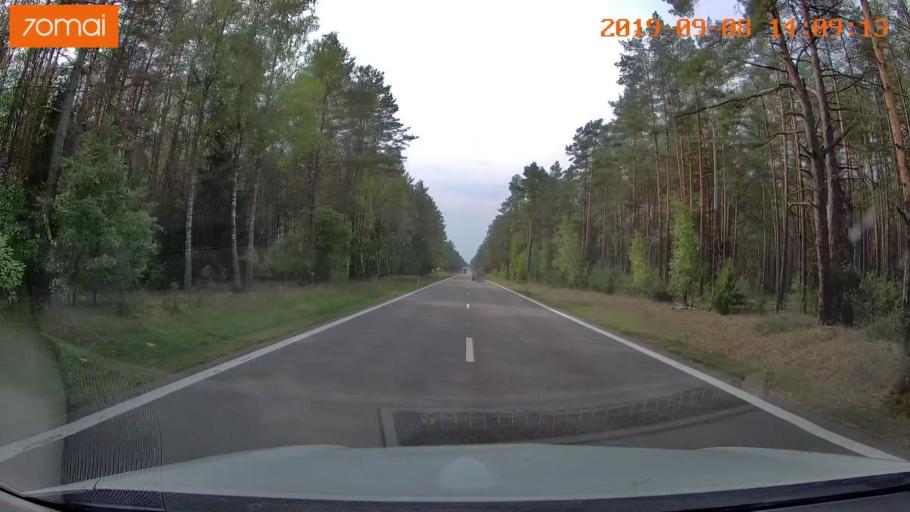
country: LT
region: Alytaus apskritis
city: Druskininkai
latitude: 54.0513
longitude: 24.1273
